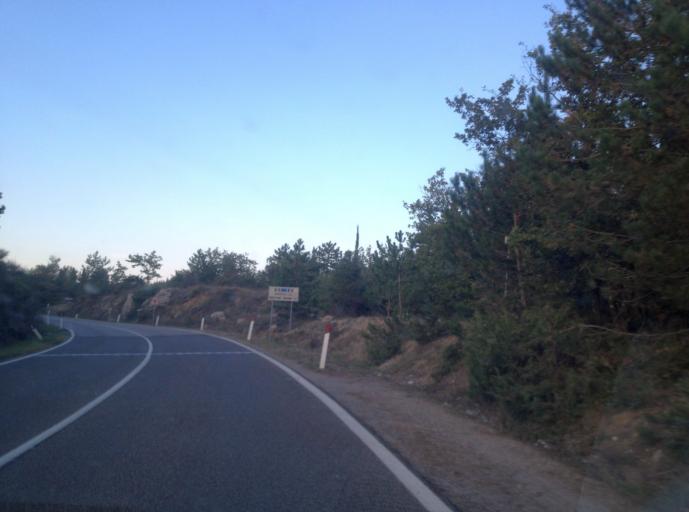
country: IT
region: Tuscany
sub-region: Provincia di Siena
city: Castellina in Chianti
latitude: 43.4532
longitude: 11.2924
